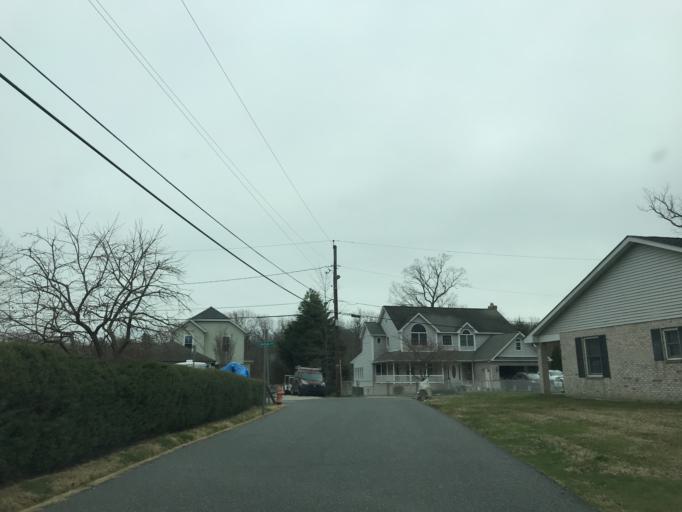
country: US
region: Maryland
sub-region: Baltimore County
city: Middle River
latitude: 39.2980
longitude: -76.4219
